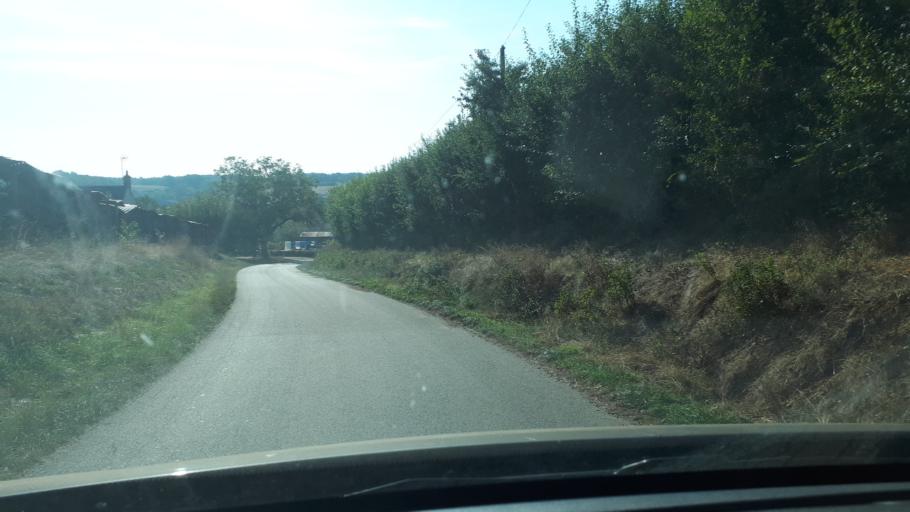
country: FR
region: Centre
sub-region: Departement du Loir-et-Cher
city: Aze
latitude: 47.8331
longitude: 0.9762
